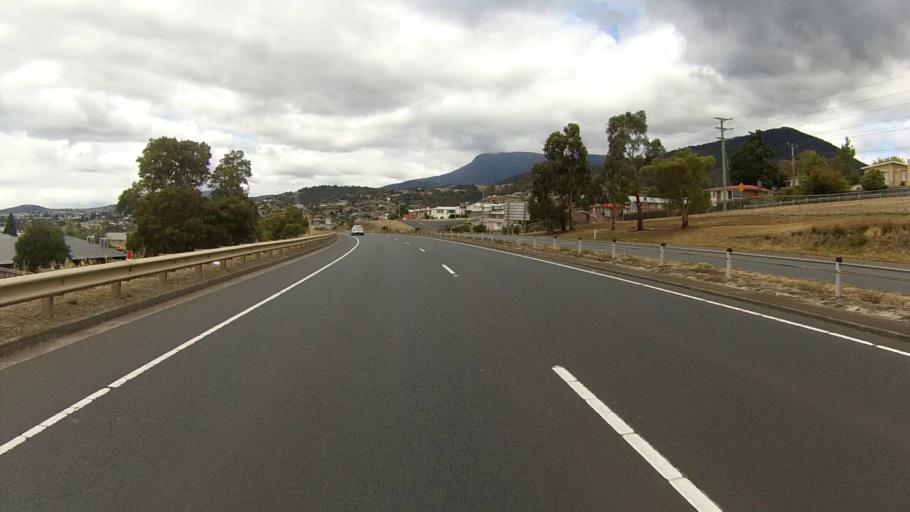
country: AU
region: Tasmania
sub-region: Glenorchy
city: Berriedale
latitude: -42.8069
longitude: 147.2489
